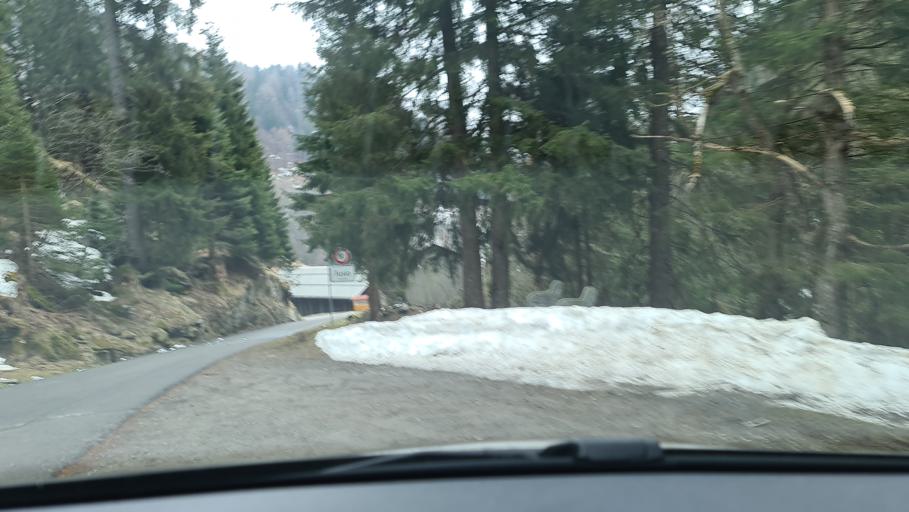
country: CH
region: Ticino
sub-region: Leventina District
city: Airolo
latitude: 46.4483
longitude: 8.6626
